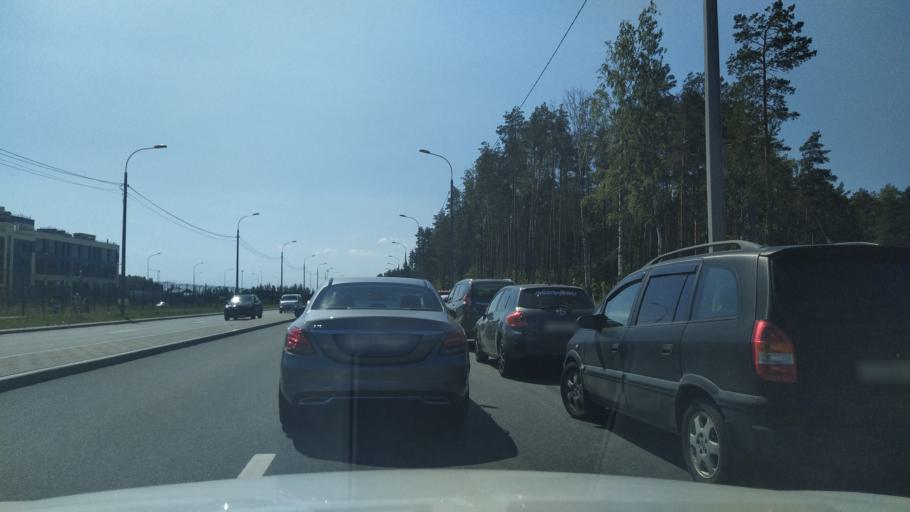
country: RU
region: Leningrad
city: Untolovo
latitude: 60.0551
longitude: 30.2335
